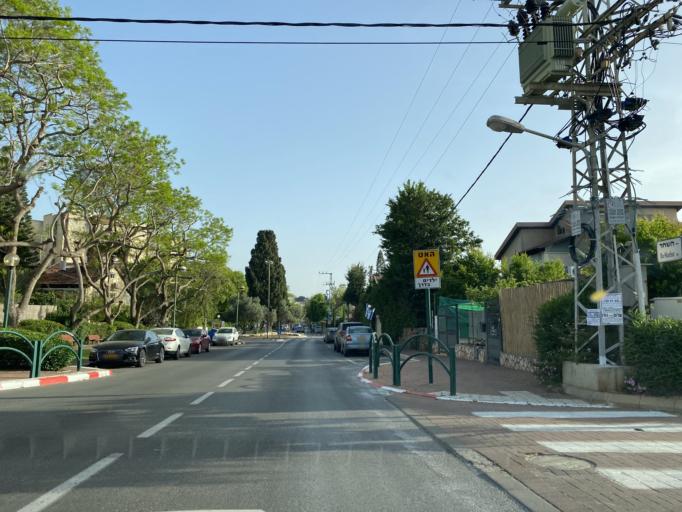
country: IL
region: Central District
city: Kfar Saba
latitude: 32.1817
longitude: 34.9101
